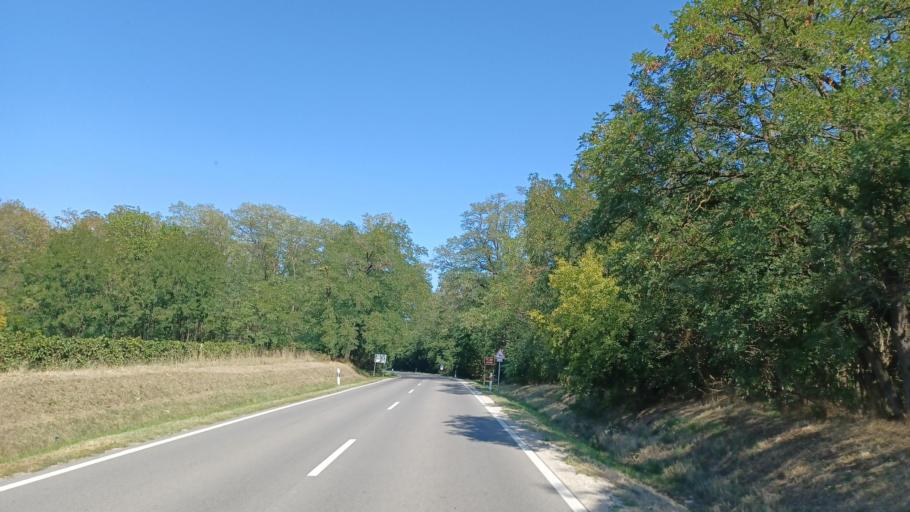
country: HU
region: Tolna
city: Nagydorog
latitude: 46.6931
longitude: 18.6730
